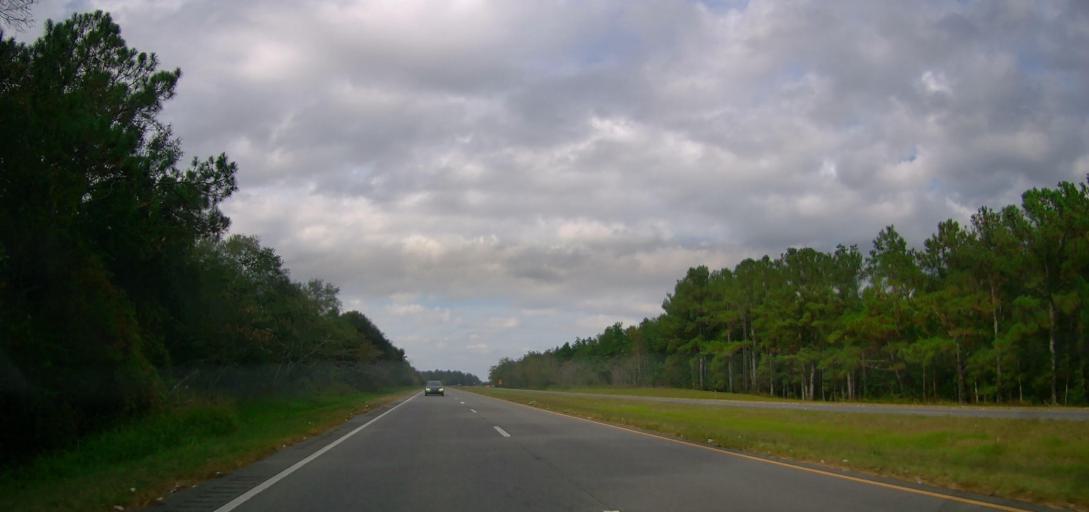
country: US
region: Georgia
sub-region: Thomas County
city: Meigs
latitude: 31.0397
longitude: -84.0671
